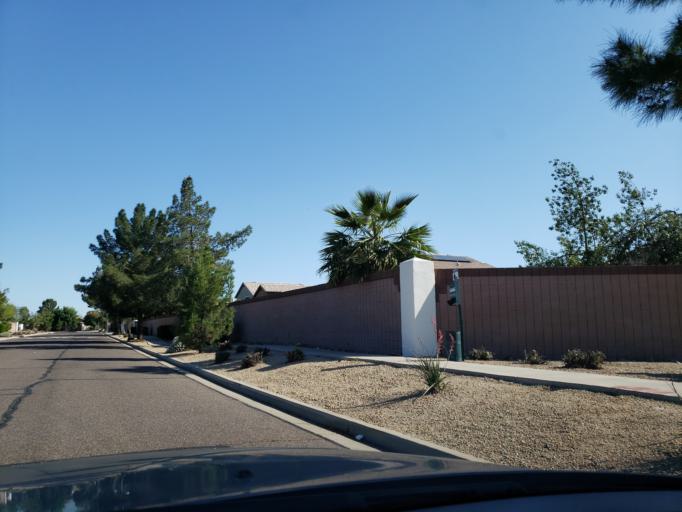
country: US
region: Arizona
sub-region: Maricopa County
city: Glendale
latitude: 33.5504
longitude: -112.1720
